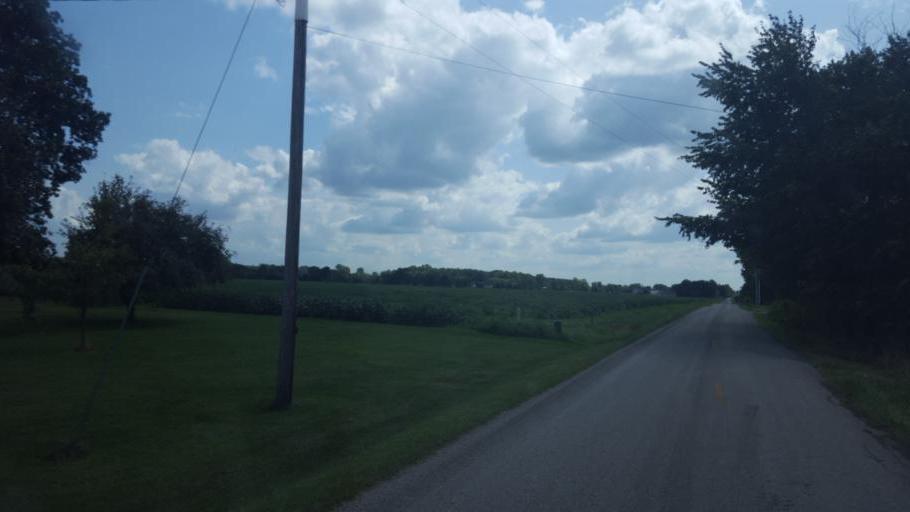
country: US
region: Ohio
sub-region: Delaware County
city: Sunbury
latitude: 40.3474
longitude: -82.8566
